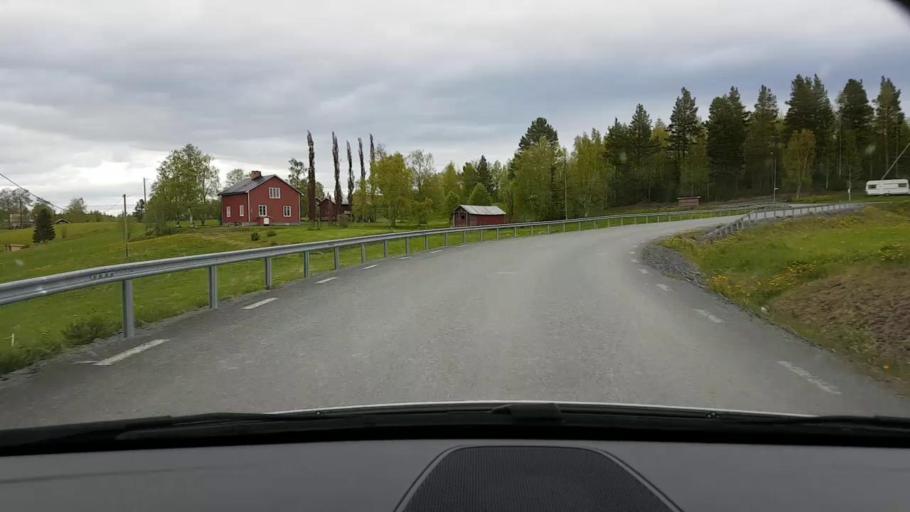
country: SE
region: Jaemtland
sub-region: Krokoms Kommun
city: Krokom
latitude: 63.2369
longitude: 14.0688
